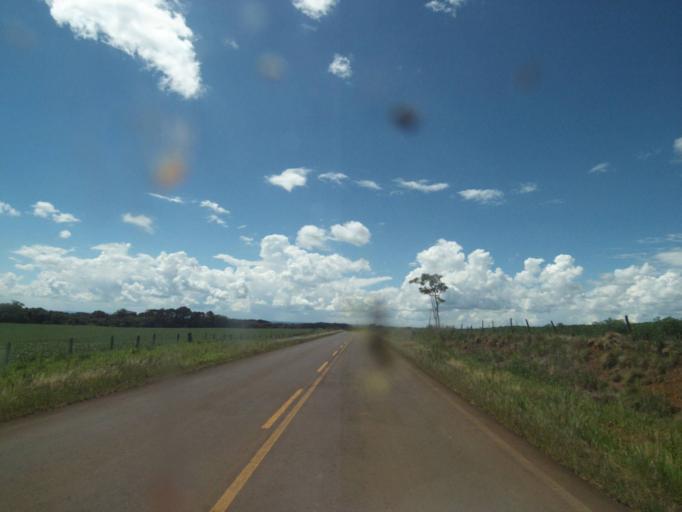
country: BR
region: Parana
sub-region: Pinhao
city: Pinhao
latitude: -25.8018
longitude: -52.0740
